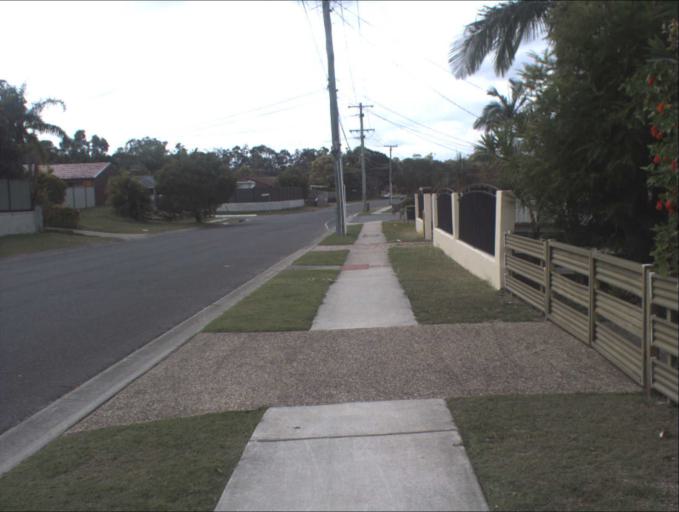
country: AU
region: Queensland
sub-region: Brisbane
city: Sunnybank Hills
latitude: -27.6691
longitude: 153.0467
